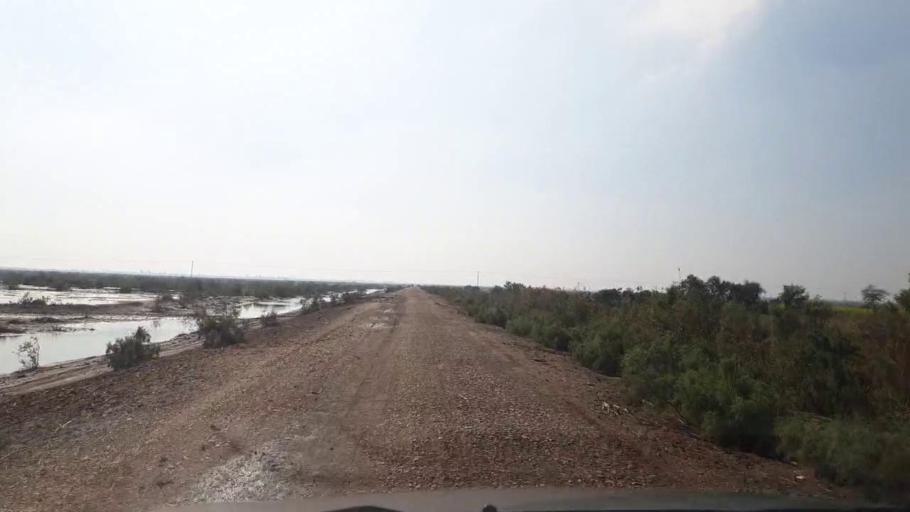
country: PK
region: Sindh
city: Sinjhoro
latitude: 26.0380
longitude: 68.7786
